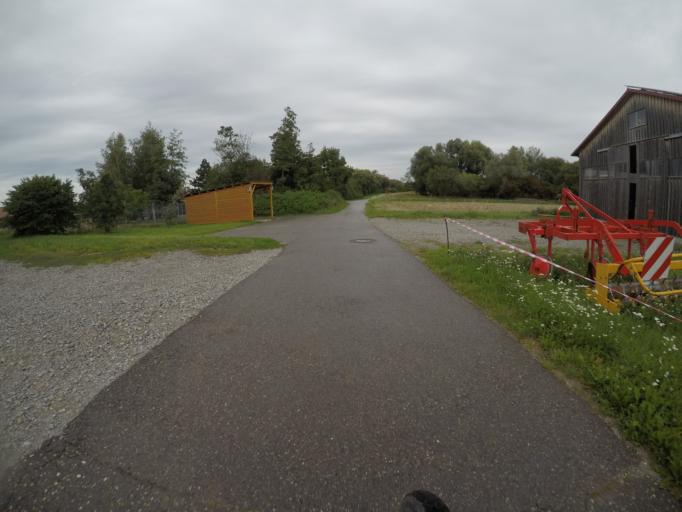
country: DE
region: Baden-Wuerttemberg
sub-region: Regierungsbezirk Stuttgart
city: Nufringen
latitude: 48.6233
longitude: 8.9080
